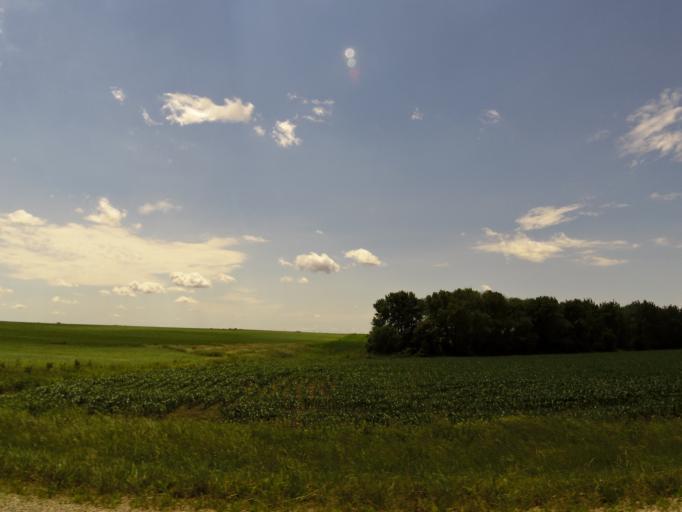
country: US
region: Iowa
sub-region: Buchanan County
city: Fairbank
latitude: 42.7148
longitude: -92.0312
